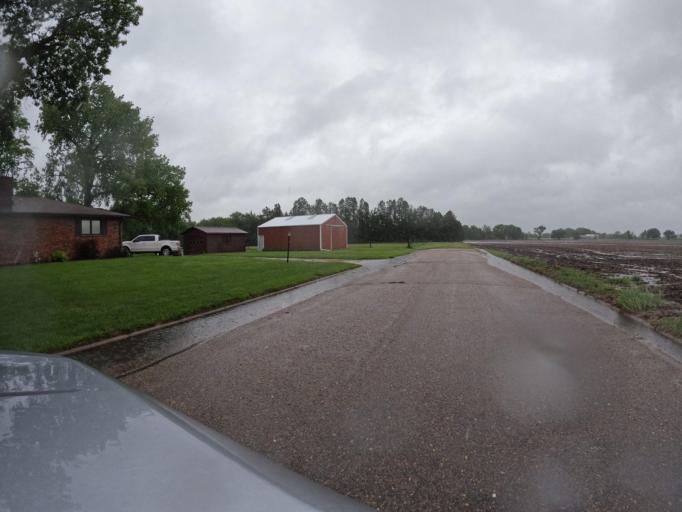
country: US
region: Nebraska
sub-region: Gage County
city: Wymore
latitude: 40.1240
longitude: -96.6772
